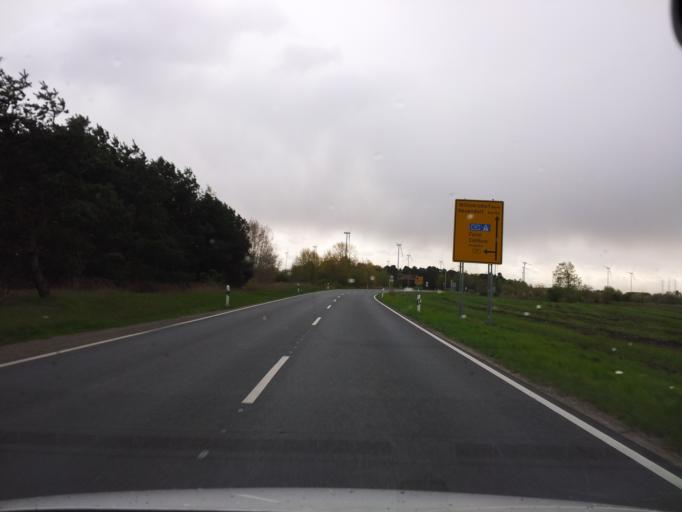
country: DE
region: Brandenburg
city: Heinersbruck
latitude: 51.8010
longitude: 14.4854
